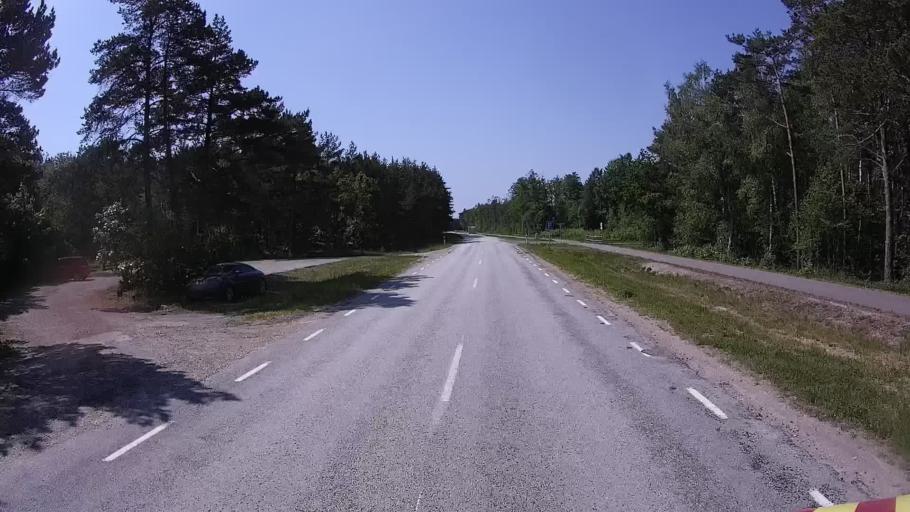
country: EE
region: Saare
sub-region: Kuressaare linn
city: Kuressaare
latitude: 58.2102
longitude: 22.3083
